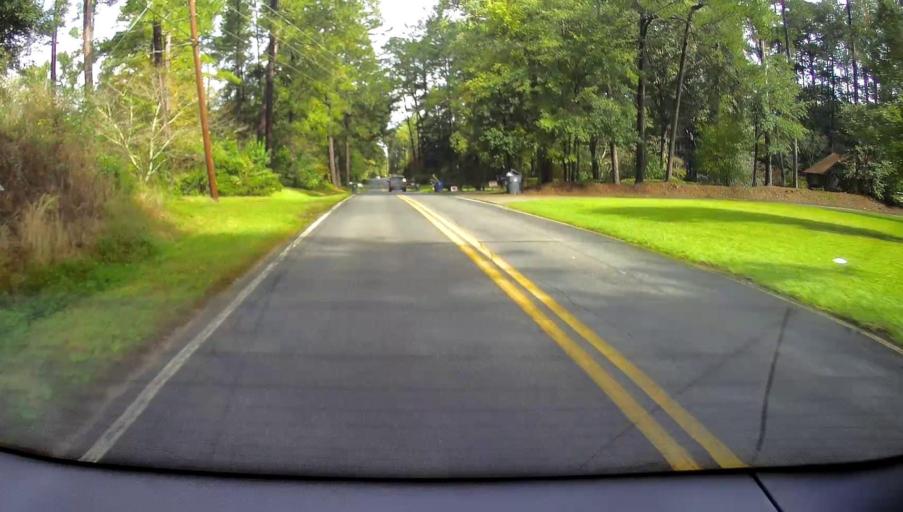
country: US
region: Georgia
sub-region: Bibb County
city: Macon
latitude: 32.9057
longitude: -83.7168
